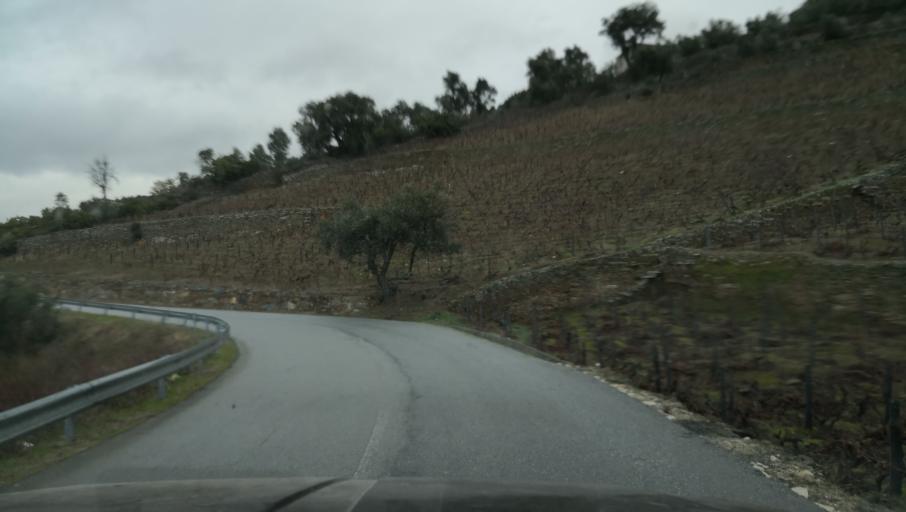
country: PT
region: Vila Real
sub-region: Santa Marta de Penaguiao
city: Santa Marta de Penaguiao
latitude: 41.2099
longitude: -7.7551
